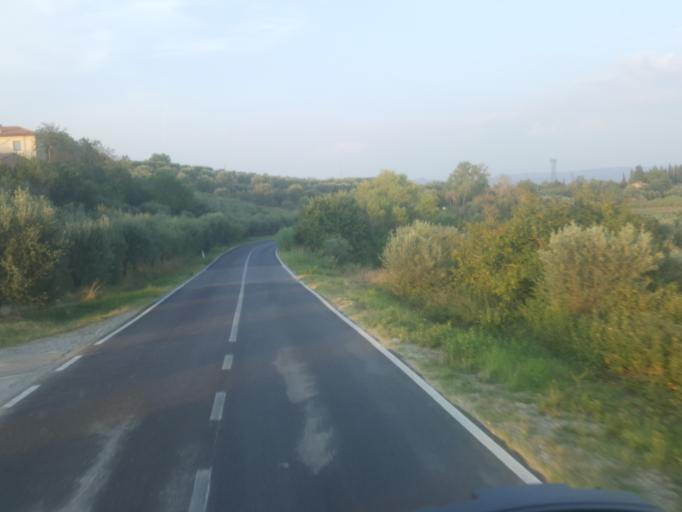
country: IT
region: Tuscany
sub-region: Province of Florence
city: Certaldo
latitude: 43.5431
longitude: 10.9964
